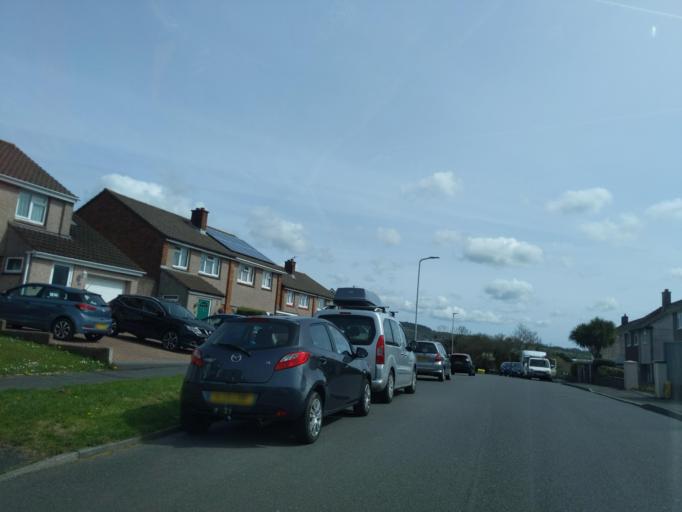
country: GB
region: England
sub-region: Devon
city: Plympton
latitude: 50.3964
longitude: -4.0533
